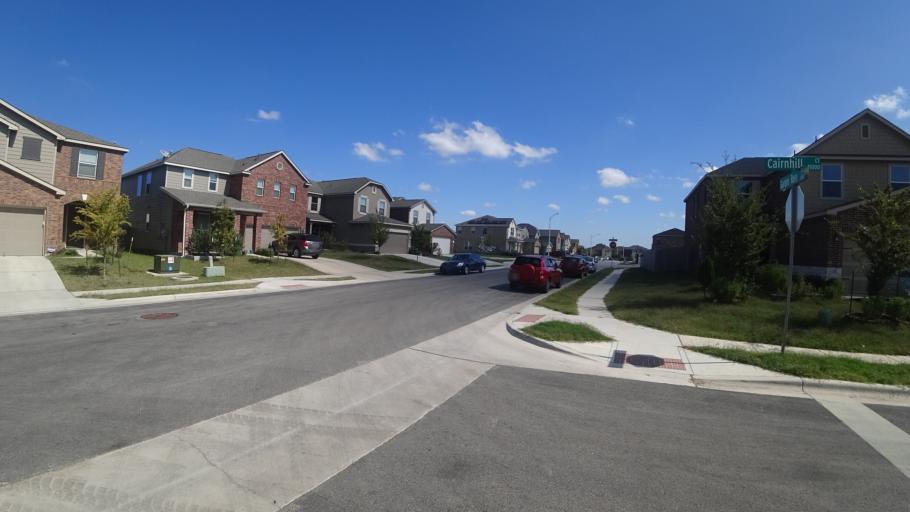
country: US
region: Texas
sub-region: Travis County
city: Manor
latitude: 30.3468
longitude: -97.6205
